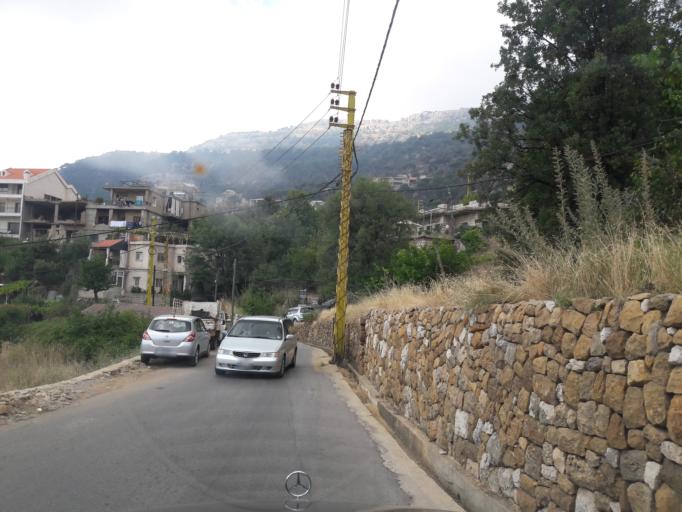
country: LB
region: Beqaa
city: Zahle
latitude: 33.9438
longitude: 35.7996
